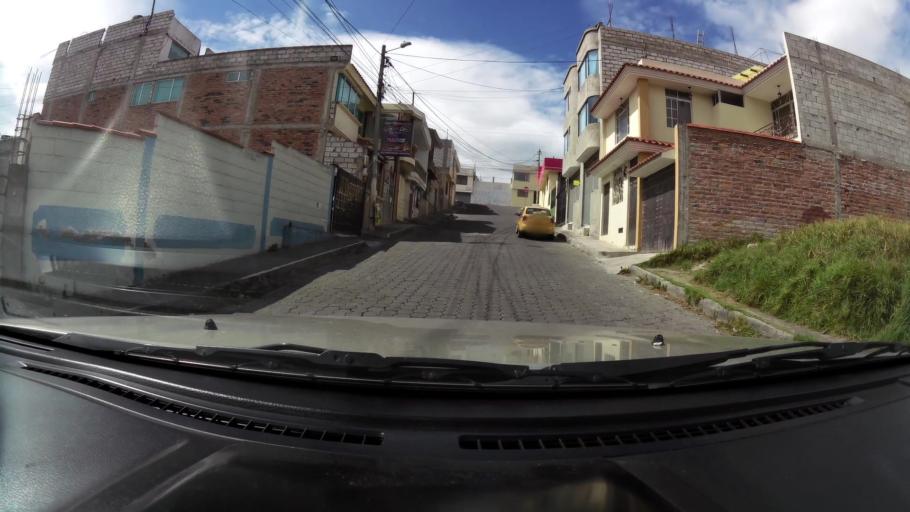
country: EC
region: Cotopaxi
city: Latacunga
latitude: -0.9287
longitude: -78.6042
